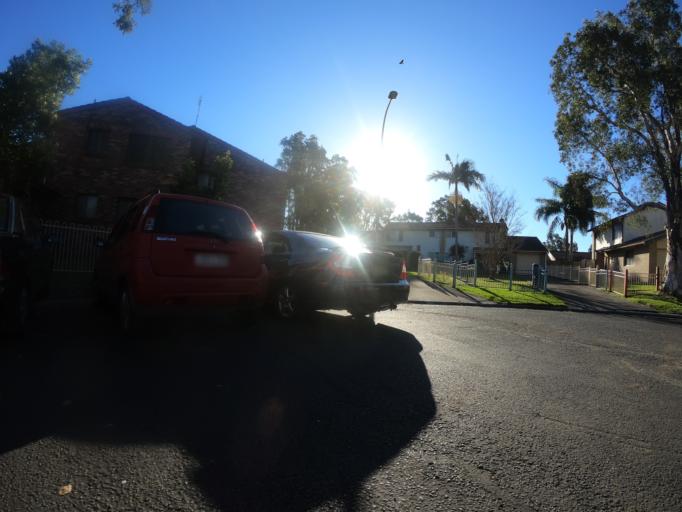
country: AU
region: New South Wales
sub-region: Wollongong
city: East Corrimal
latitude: -34.3685
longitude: 150.9192
